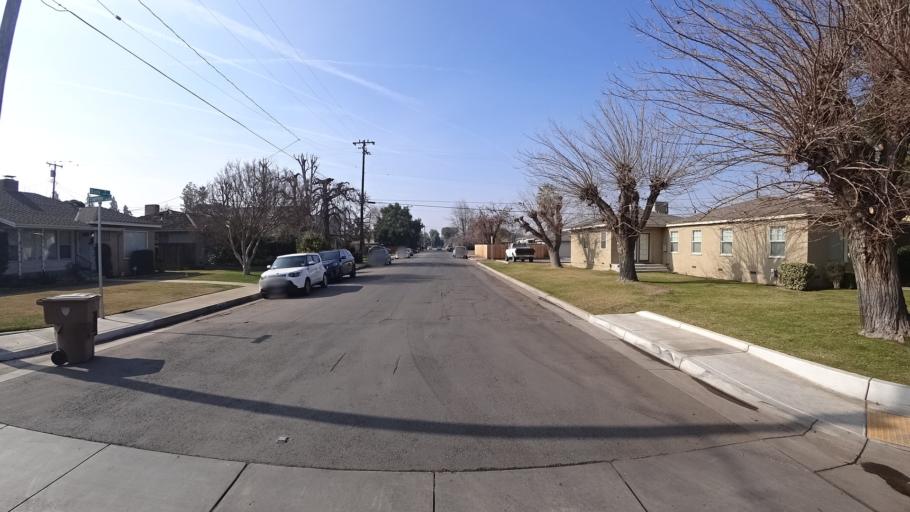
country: US
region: California
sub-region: Kern County
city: Bakersfield
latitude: 35.3580
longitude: -119.0362
